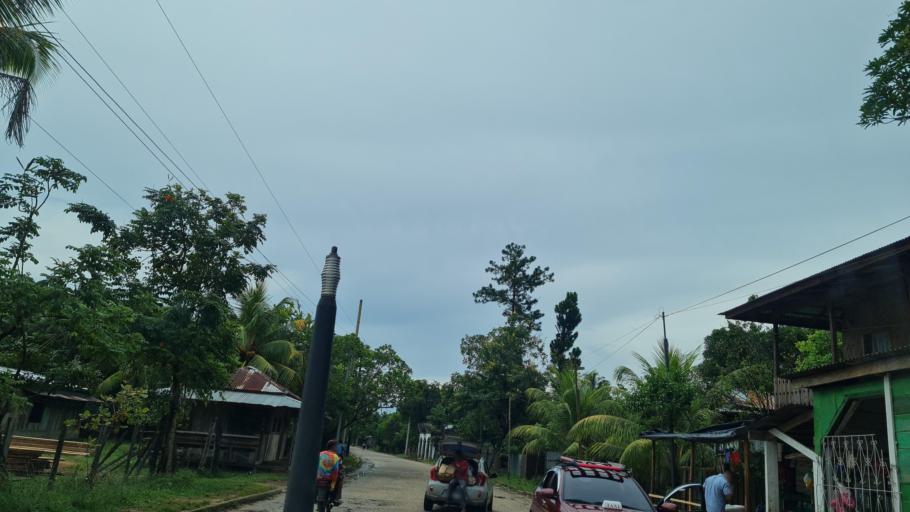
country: NI
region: Atlantico Norte (RAAN)
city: Waspam
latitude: 14.7310
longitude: -83.9691
